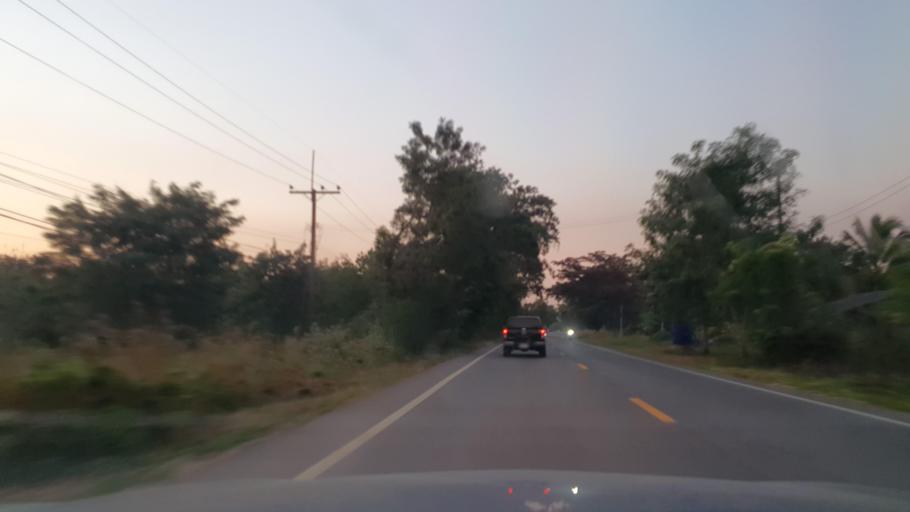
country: TH
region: Phayao
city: Dok Kham Tai
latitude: 19.1342
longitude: 100.0256
